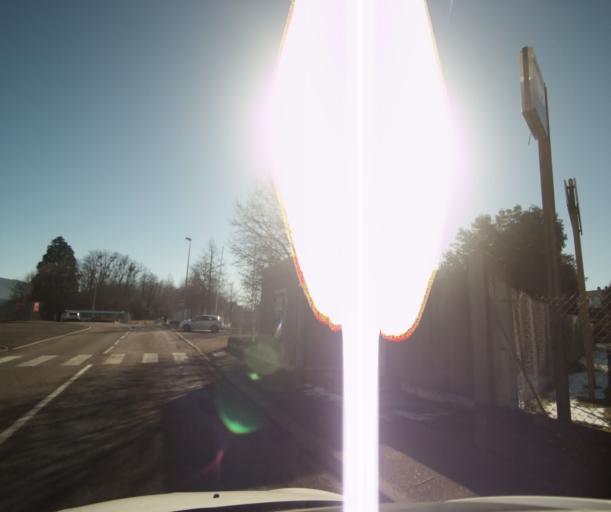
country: FR
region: Franche-Comte
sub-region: Departement du Doubs
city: Thise
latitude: 47.2658
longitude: 6.0504
